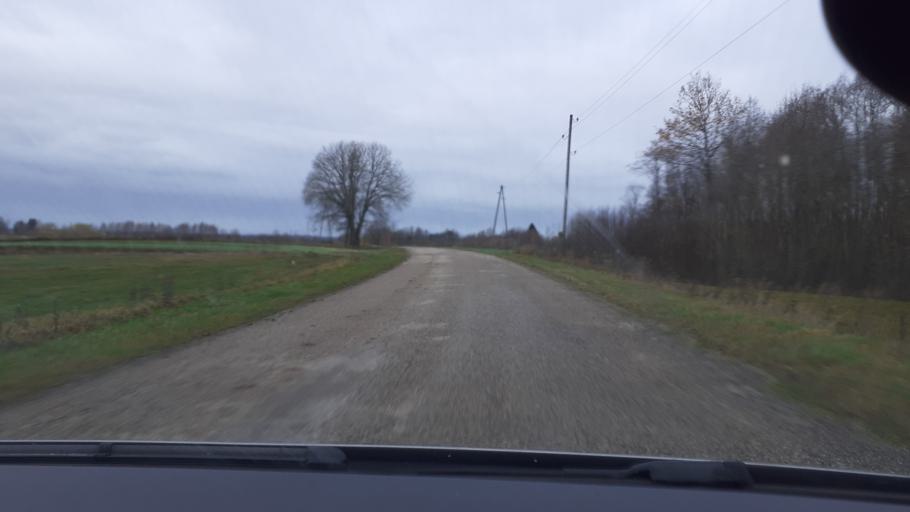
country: LV
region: Aizpute
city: Aizpute
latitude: 56.7757
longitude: 21.7819
